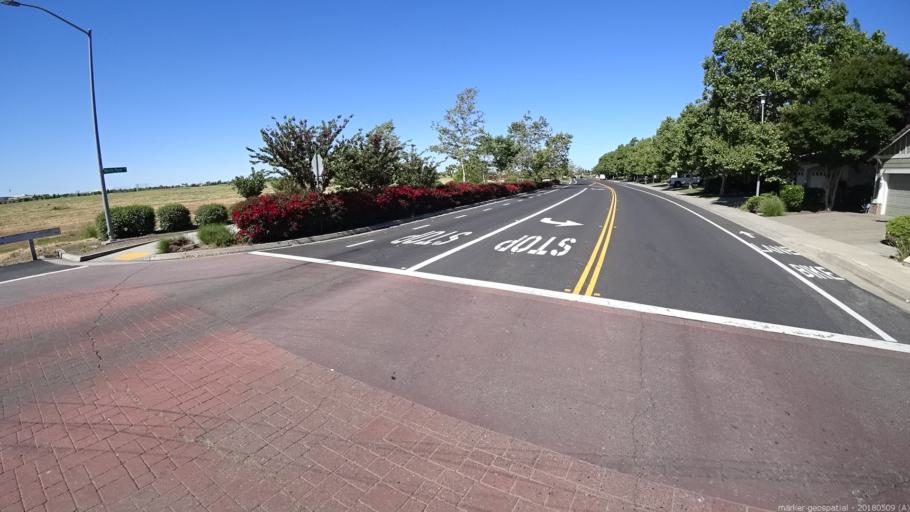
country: US
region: California
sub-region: Sacramento County
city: Elverta
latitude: 38.6663
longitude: -121.5174
